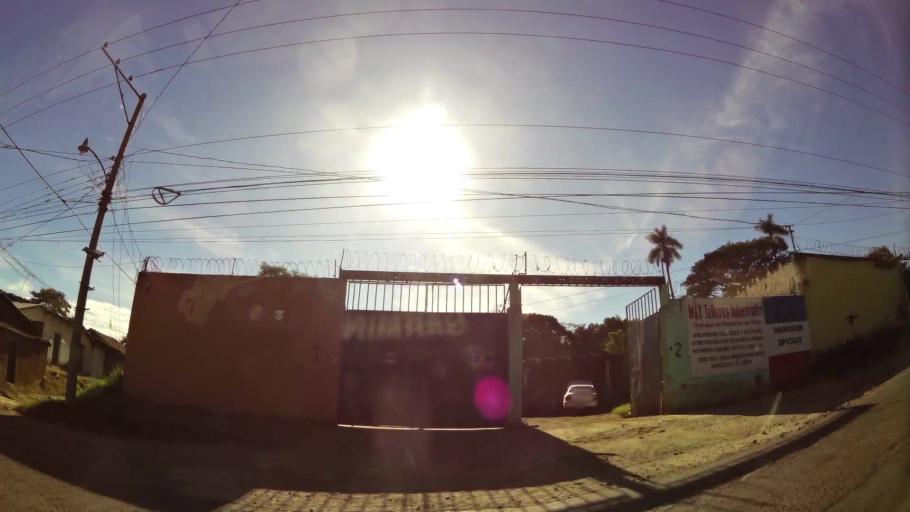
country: SV
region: Santa Ana
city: Santa Ana
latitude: 13.9790
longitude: -89.5784
